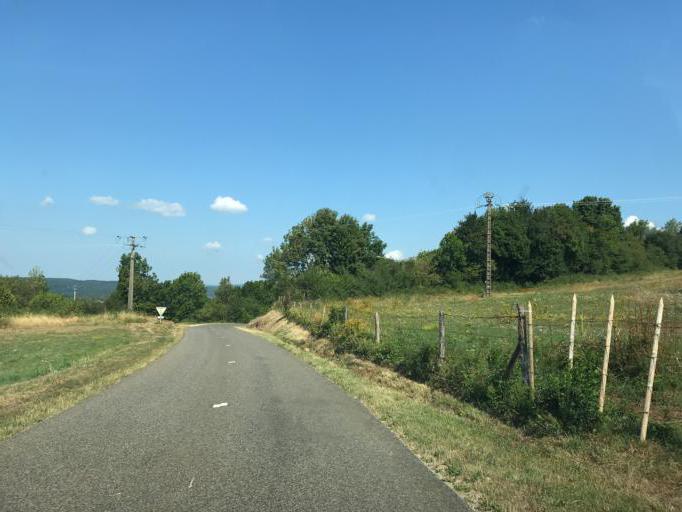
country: FR
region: Franche-Comte
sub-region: Departement du Jura
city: Moirans-en-Montagne
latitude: 46.4587
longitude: 5.7336
